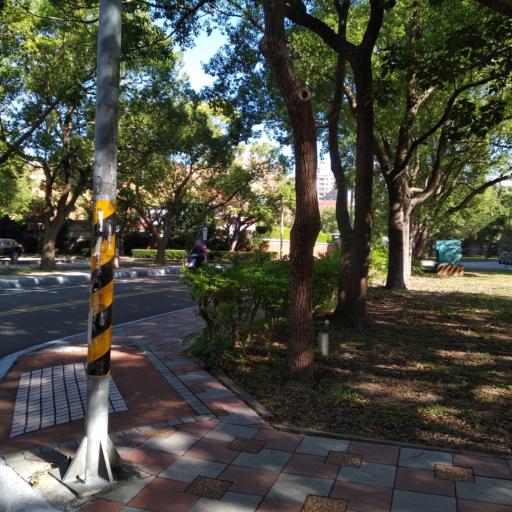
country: TW
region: Taiwan
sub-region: Hsinchu
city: Zhubei
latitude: 24.8269
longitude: 121.0139
